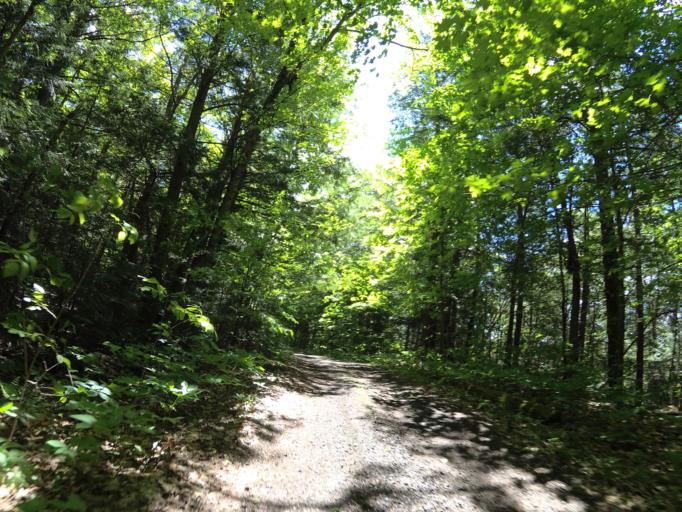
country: CA
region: Ontario
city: Renfrew
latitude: 45.0504
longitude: -76.8368
